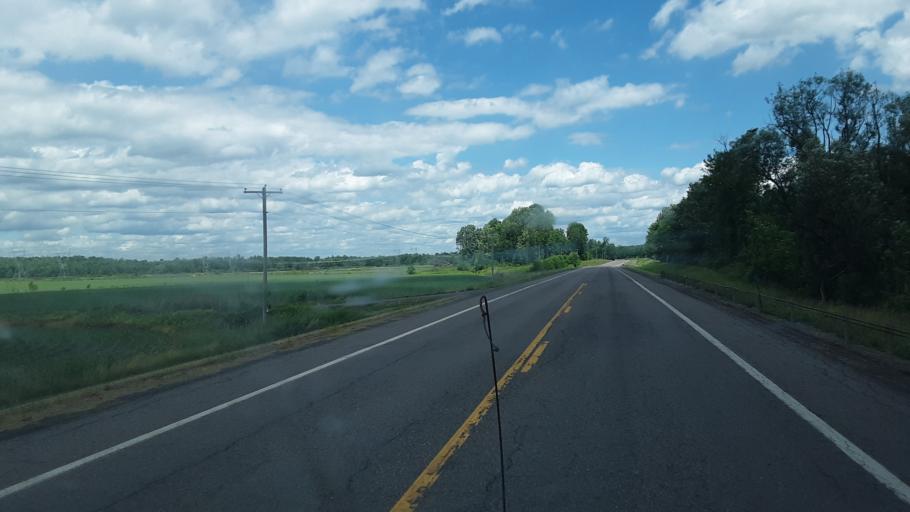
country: US
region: New York
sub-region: Madison County
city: Oneida
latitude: 43.1632
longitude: -75.6604
